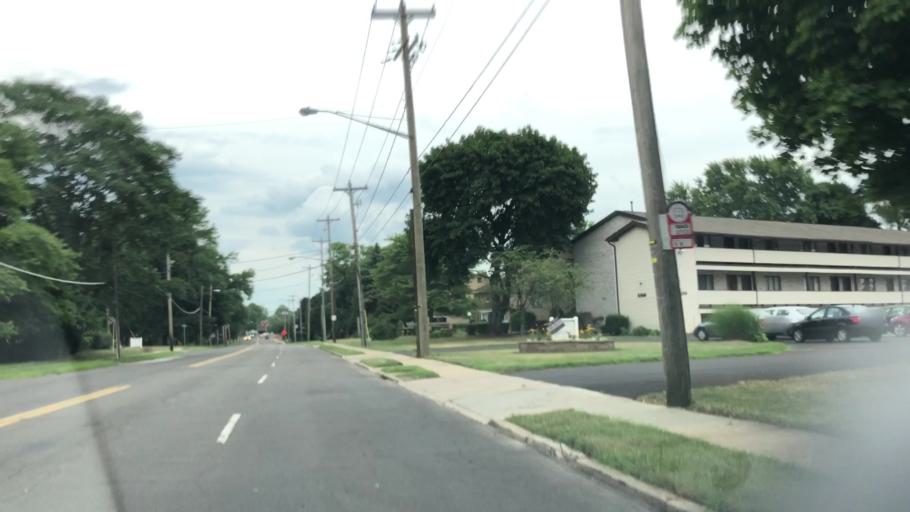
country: US
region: Ohio
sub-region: Summit County
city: Sawyerwood
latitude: 41.0569
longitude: -81.4450
